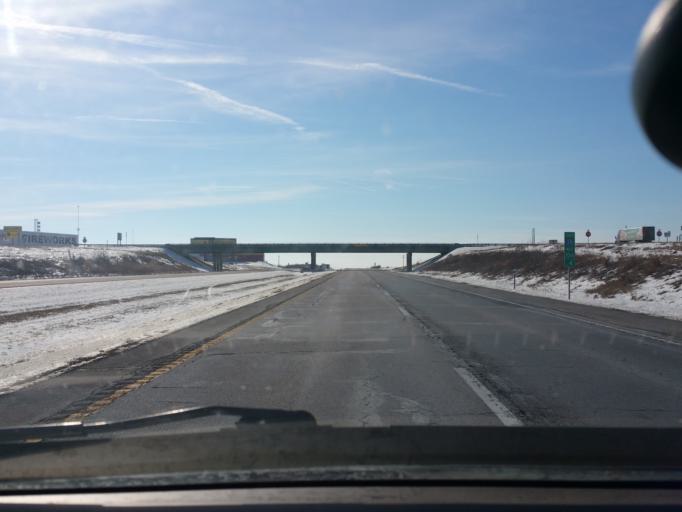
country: US
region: Iowa
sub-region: Decatur County
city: Lamoni
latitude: 40.4682
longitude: -93.9766
